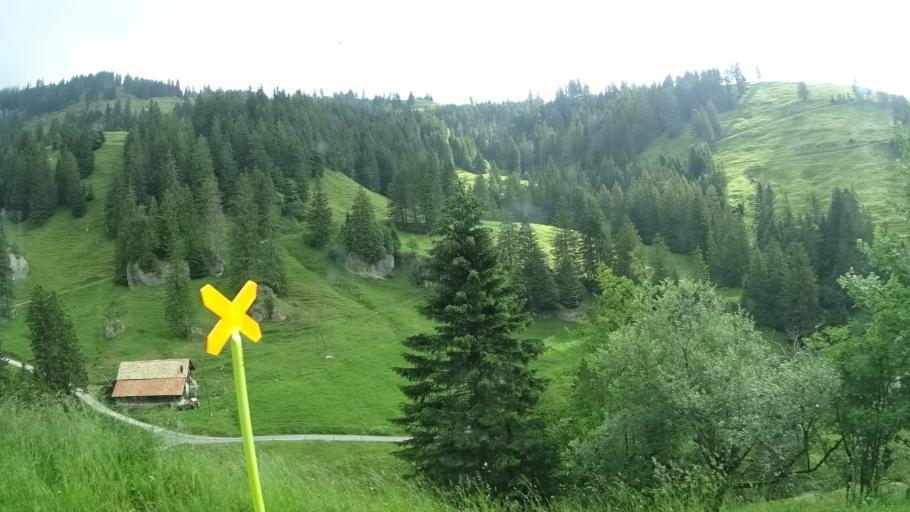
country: CH
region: Lucerne
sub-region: Lucerne-Land District
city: Vitznau
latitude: 47.0420
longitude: 8.4885
